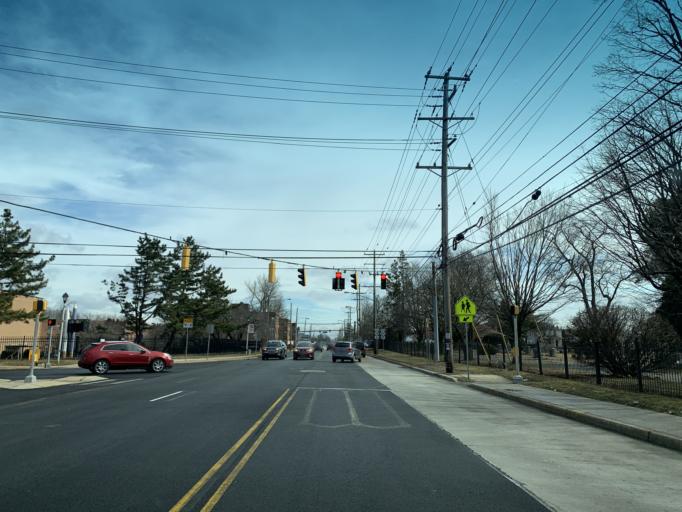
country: US
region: Delaware
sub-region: New Castle County
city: Elsmere
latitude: 39.7526
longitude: -75.5888
